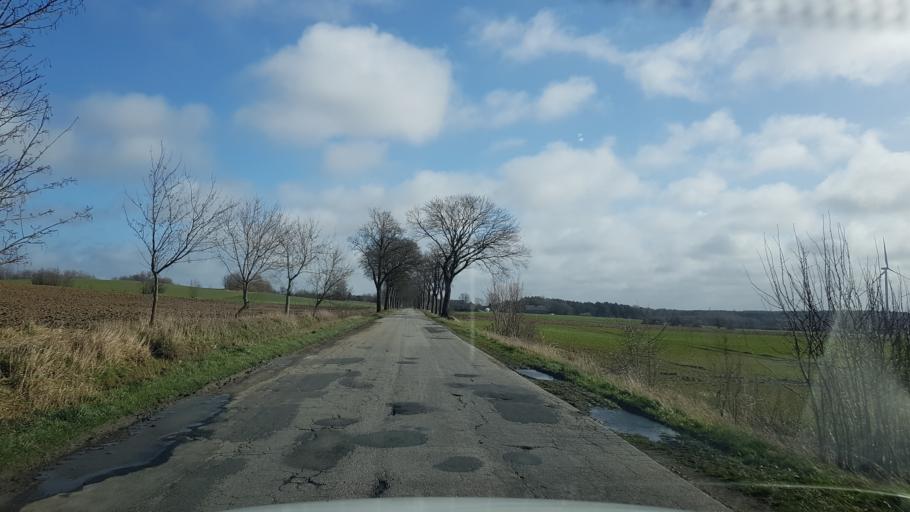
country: PL
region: West Pomeranian Voivodeship
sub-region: Powiat slawienski
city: Slawno
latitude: 54.4725
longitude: 16.6017
